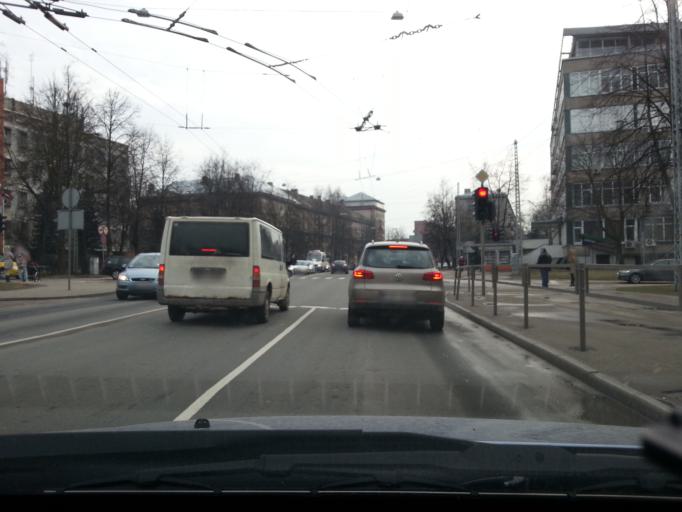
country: LV
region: Riga
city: Riga
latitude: 56.9741
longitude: 24.1353
